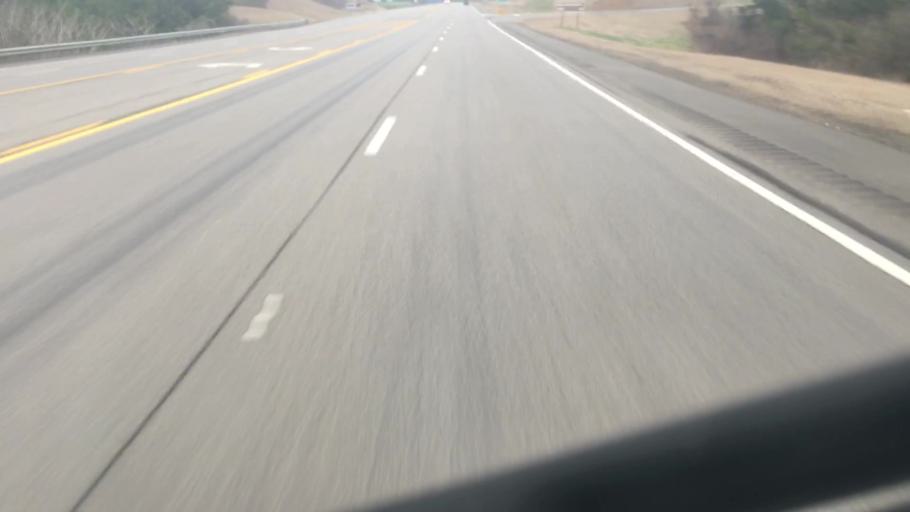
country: US
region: Alabama
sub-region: Walker County
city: Jasper
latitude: 33.8055
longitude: -87.2350
